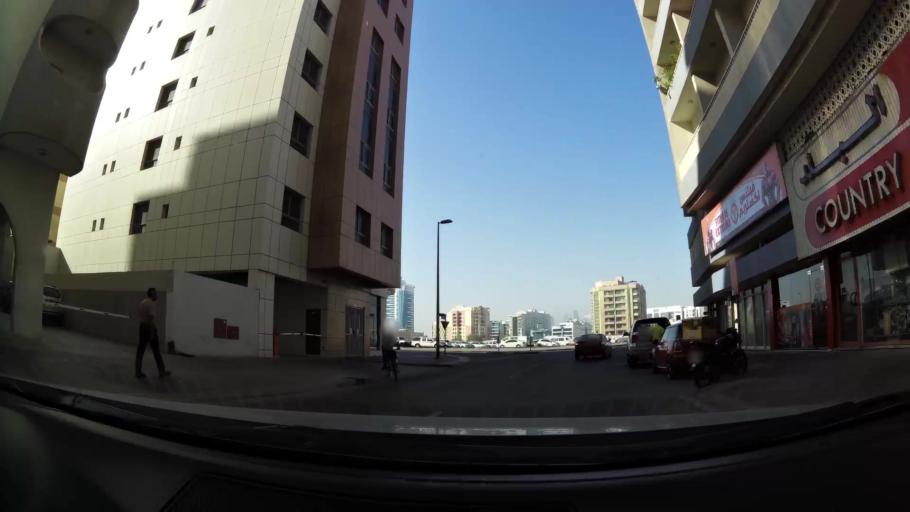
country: AE
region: Ash Shariqah
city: Sharjah
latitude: 25.2571
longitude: 55.2872
